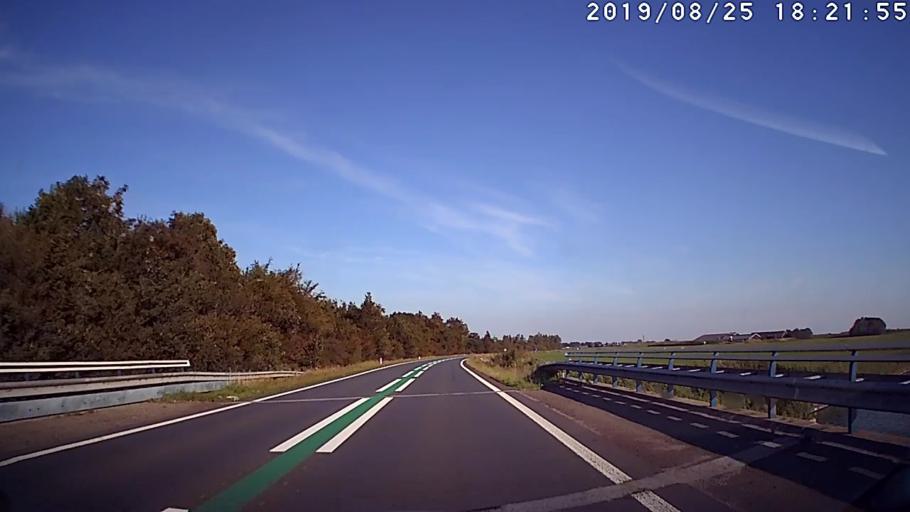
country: NL
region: Friesland
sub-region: Gemeente Gaasterlan-Sleat
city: Balk
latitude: 52.8694
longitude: 5.6404
